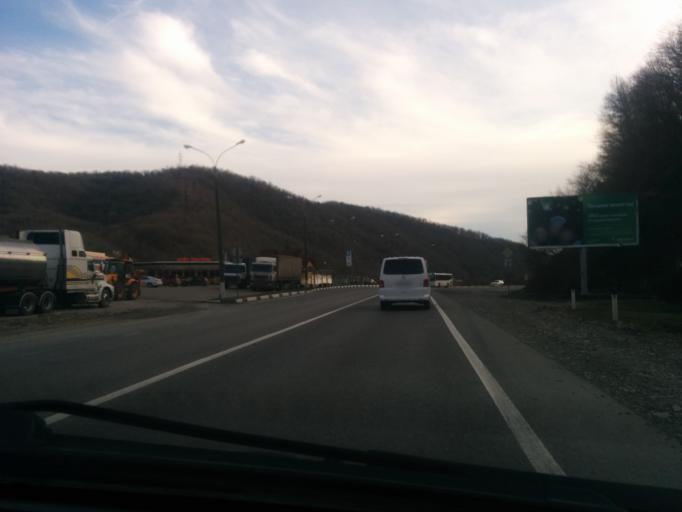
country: RU
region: Krasnodarskiy
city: Ol'ginka
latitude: 44.2147
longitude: 38.8947
